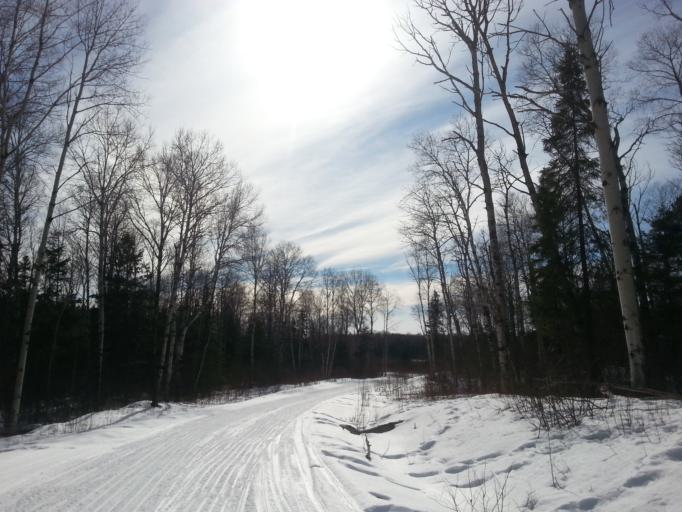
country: CA
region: Ontario
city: Greater Sudbury
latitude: 46.3306
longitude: -80.9058
